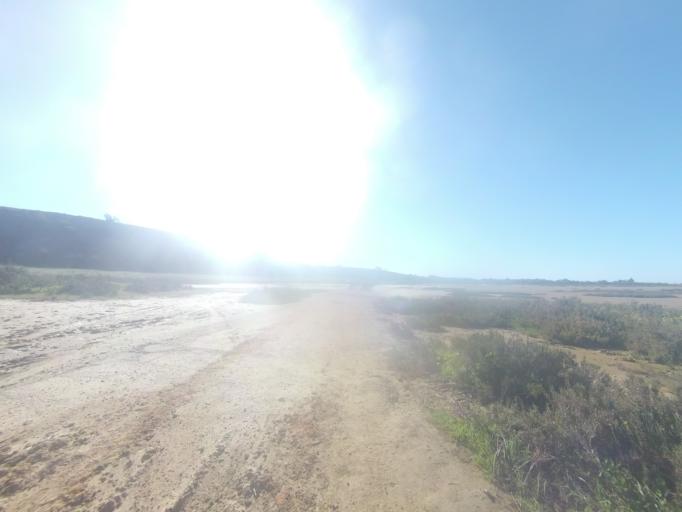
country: ES
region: Andalusia
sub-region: Provincia de Huelva
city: Palos de la Frontera
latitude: 37.2394
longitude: -6.8916
